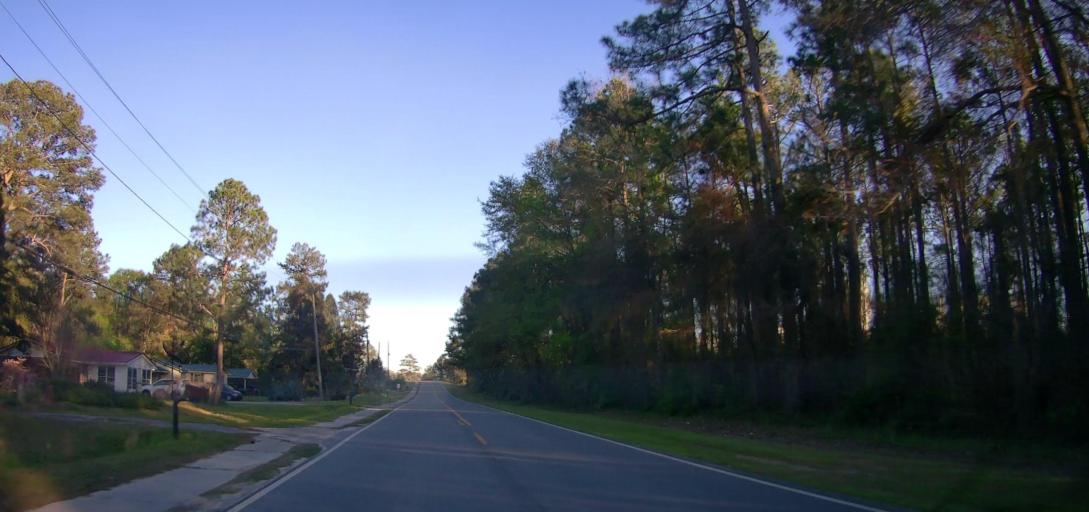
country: US
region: Georgia
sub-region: Wilkinson County
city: Irwinton
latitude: 32.8482
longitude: -83.2138
